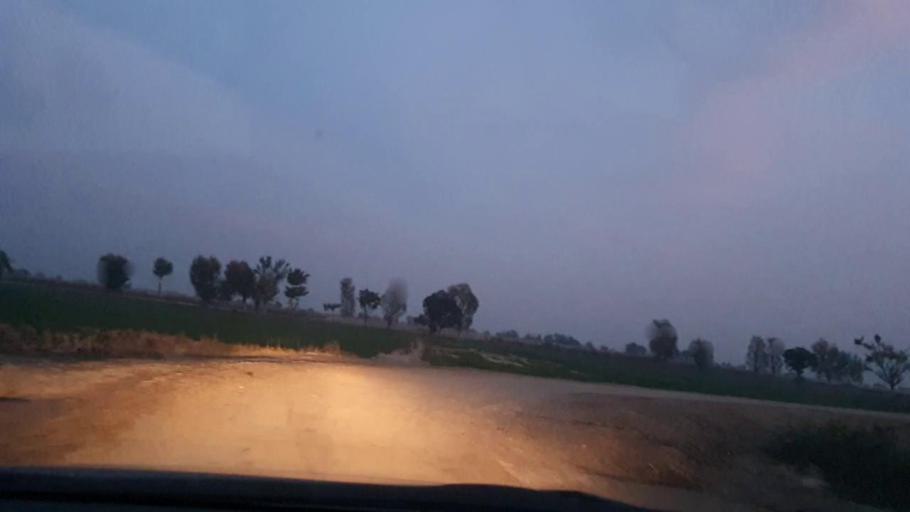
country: PK
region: Sindh
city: Sakrand
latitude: 26.1872
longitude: 68.3037
